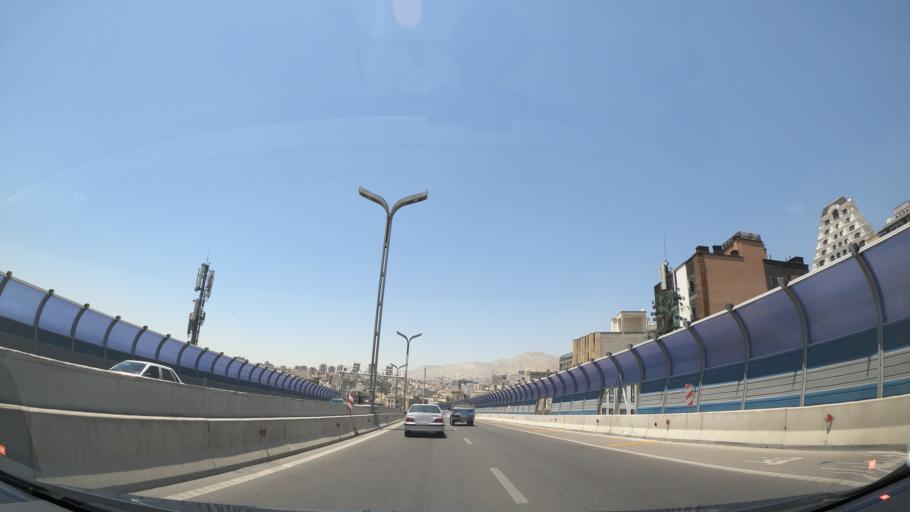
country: IR
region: Tehran
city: Tajrish
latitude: 35.7929
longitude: 51.4616
